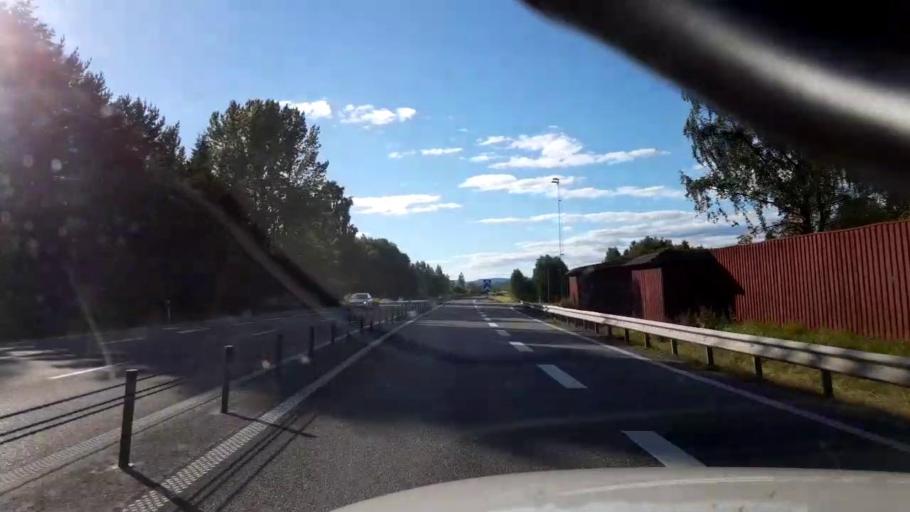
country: SE
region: Dalarna
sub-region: Borlange Kommun
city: Ornas
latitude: 60.4351
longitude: 15.5137
